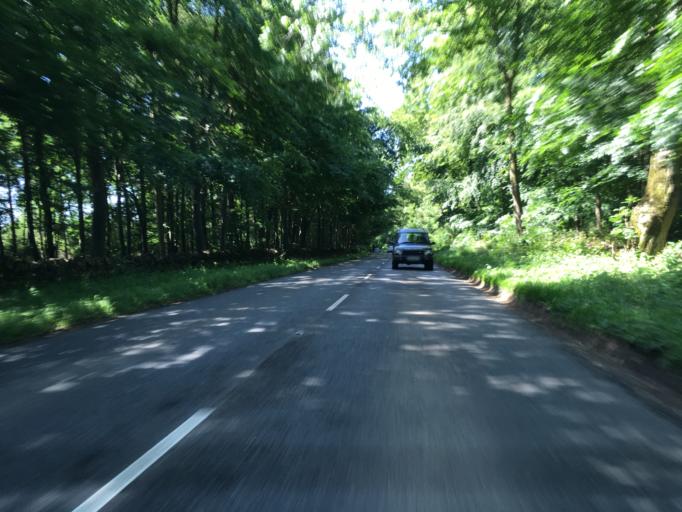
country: GB
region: England
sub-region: Oxfordshire
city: Chipping Norton
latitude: 51.9454
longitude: -1.6278
